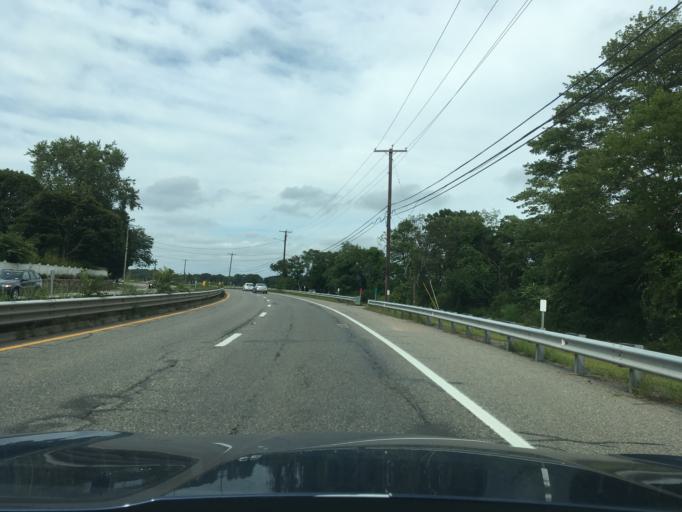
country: US
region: Rhode Island
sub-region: Bristol County
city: Barrington
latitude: 41.7611
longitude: -71.3222
